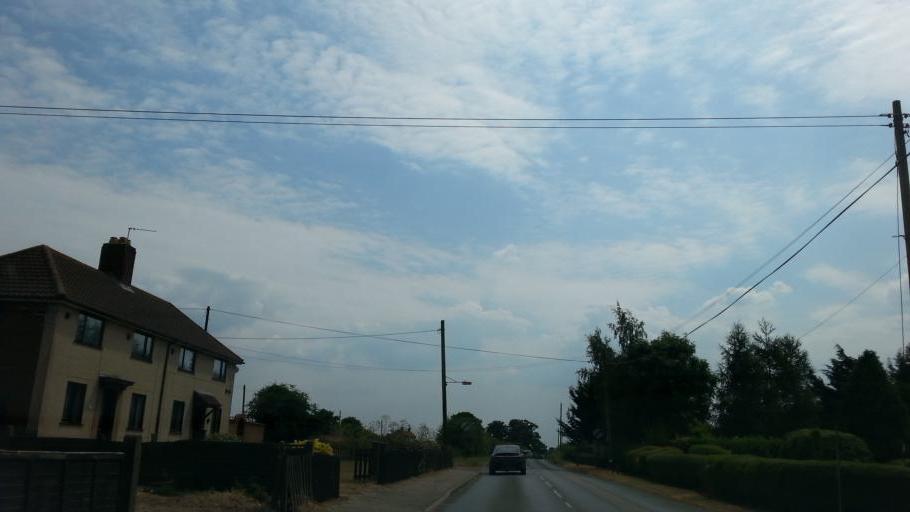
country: GB
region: England
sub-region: Suffolk
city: Lakenheath
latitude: 52.4044
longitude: 0.5277
